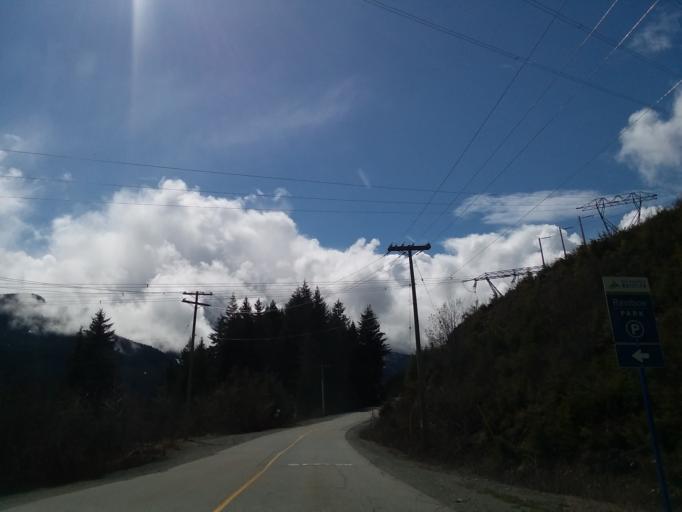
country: CA
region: British Columbia
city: Whistler
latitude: 50.1218
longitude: -122.9859
